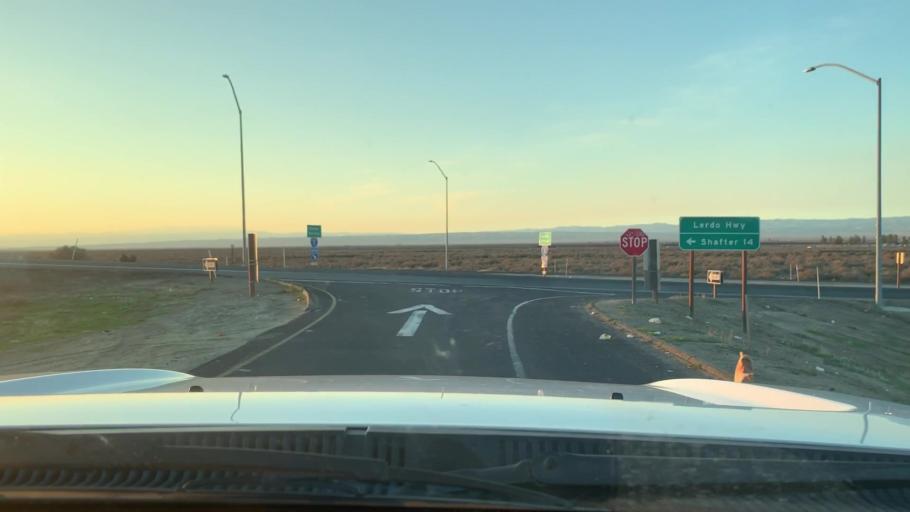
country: US
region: California
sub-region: Kern County
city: Buttonwillow
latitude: 35.5004
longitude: -119.5372
